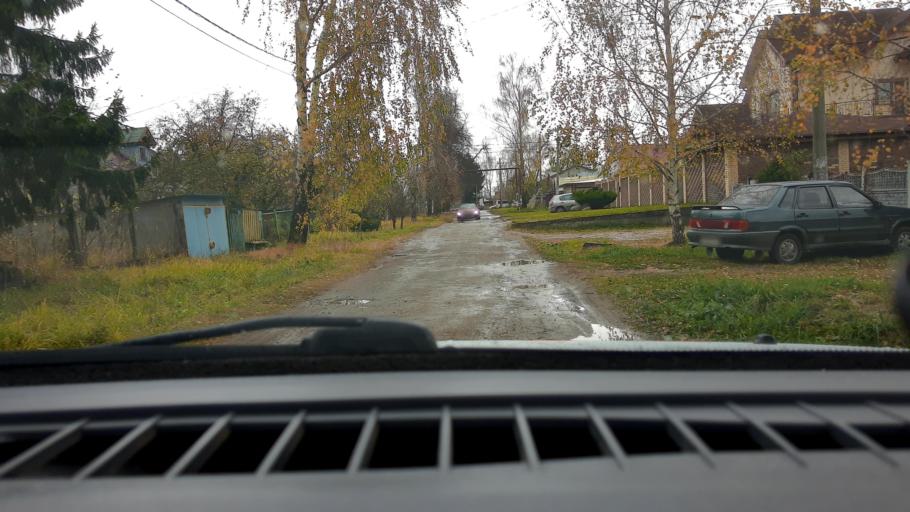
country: RU
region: Nizjnij Novgorod
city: Burevestnik
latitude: 56.2131
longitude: 43.8307
